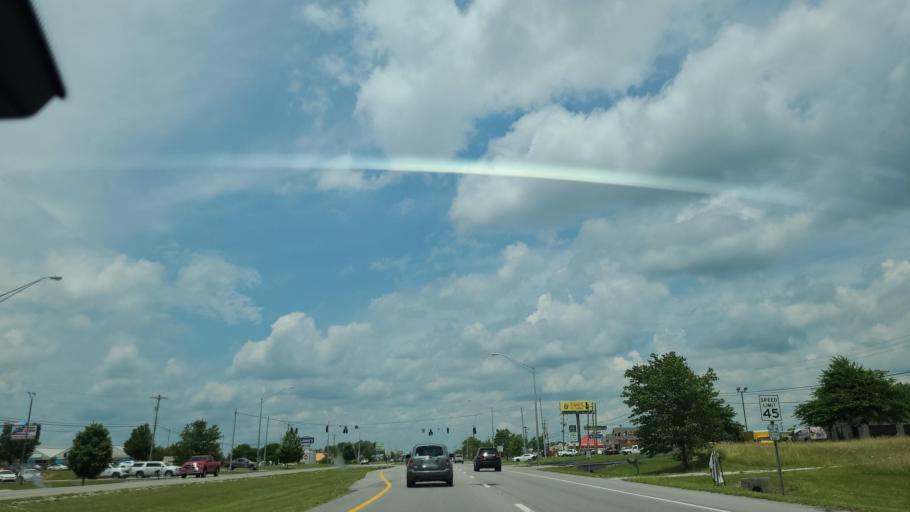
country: US
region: Tennessee
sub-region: Cumberland County
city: Crossville
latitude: 35.9777
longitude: -85.0384
